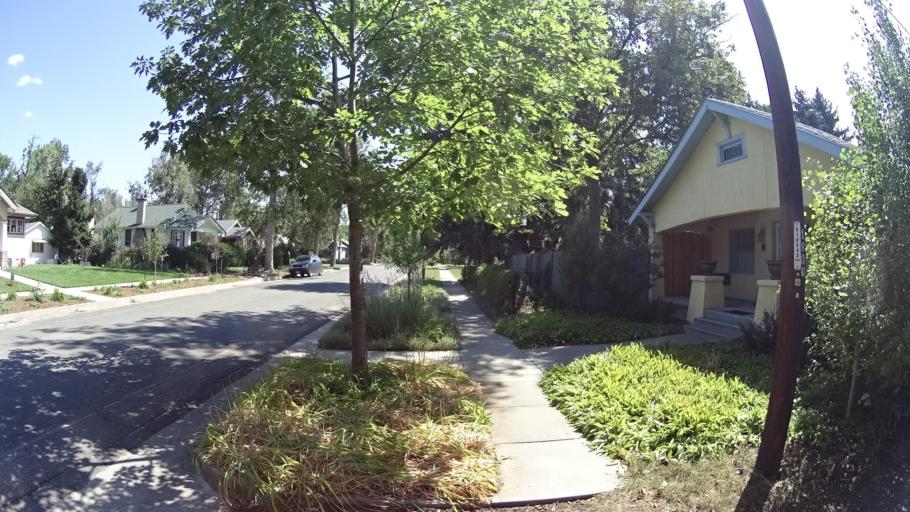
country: US
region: Colorado
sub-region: El Paso County
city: Colorado Springs
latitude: 38.8616
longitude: -104.8141
